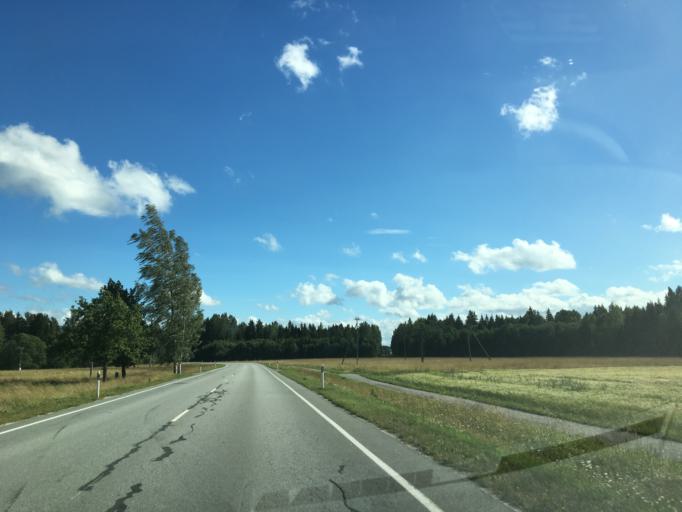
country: EE
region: Paernumaa
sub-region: Vaendra vald (alev)
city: Vandra
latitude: 58.6311
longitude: 25.0997
